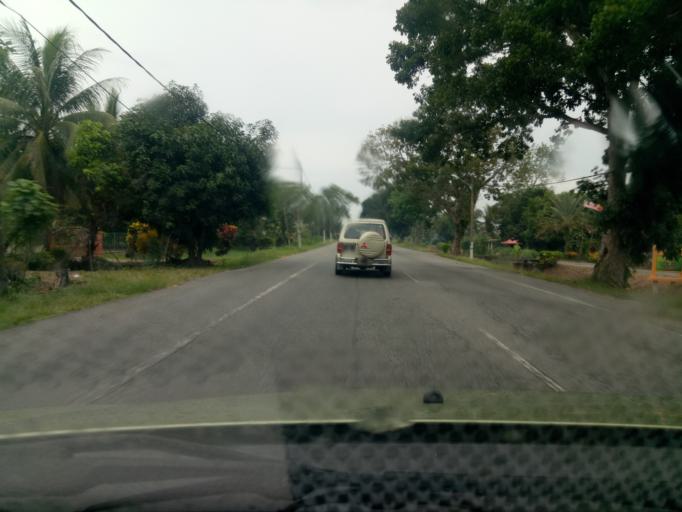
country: MY
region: Kedah
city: Gurun
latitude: 5.8952
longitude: 100.4386
